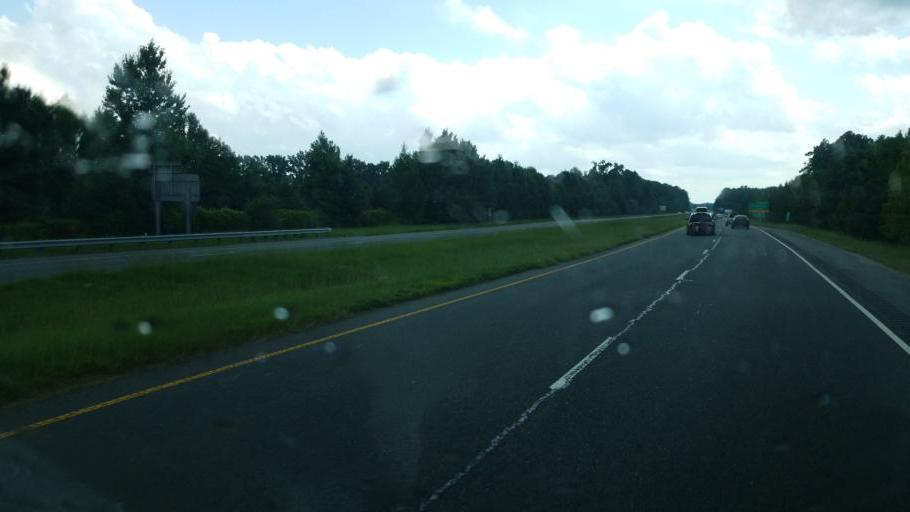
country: US
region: Virginia
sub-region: City of Chesapeake
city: Chesapeake
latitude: 36.6721
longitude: -76.2306
